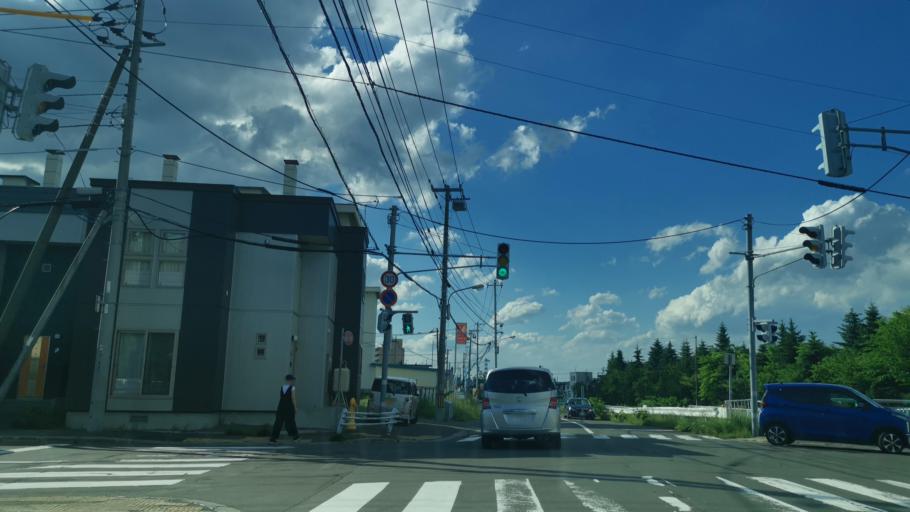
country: JP
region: Hokkaido
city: Sapporo
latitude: 43.0867
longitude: 141.2684
